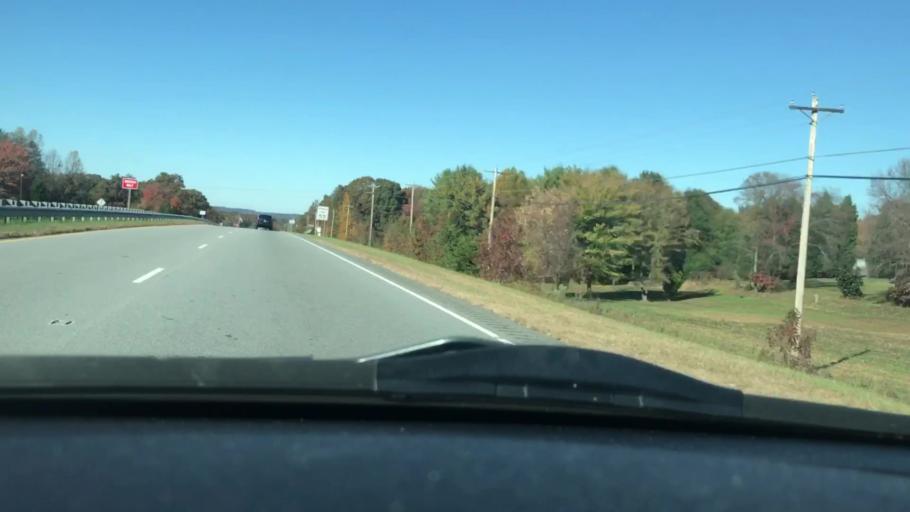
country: US
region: North Carolina
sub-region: Rockingham County
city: Madison
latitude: 36.3454
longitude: -79.9444
